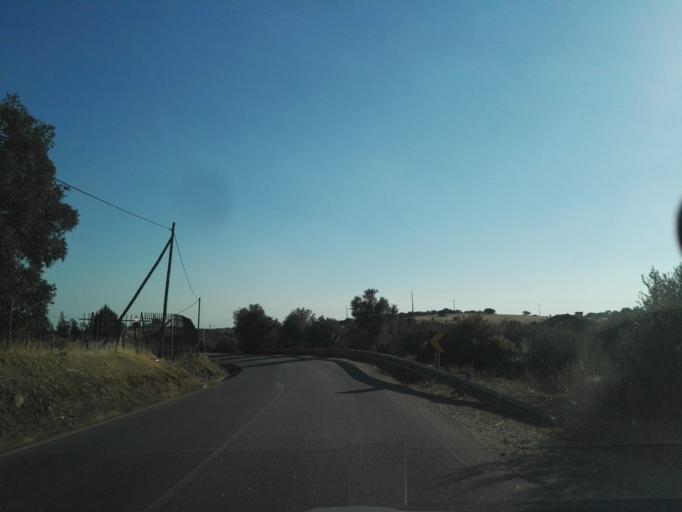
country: PT
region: Portalegre
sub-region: Elvas
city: Elvas
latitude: 38.9019
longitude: -7.1793
